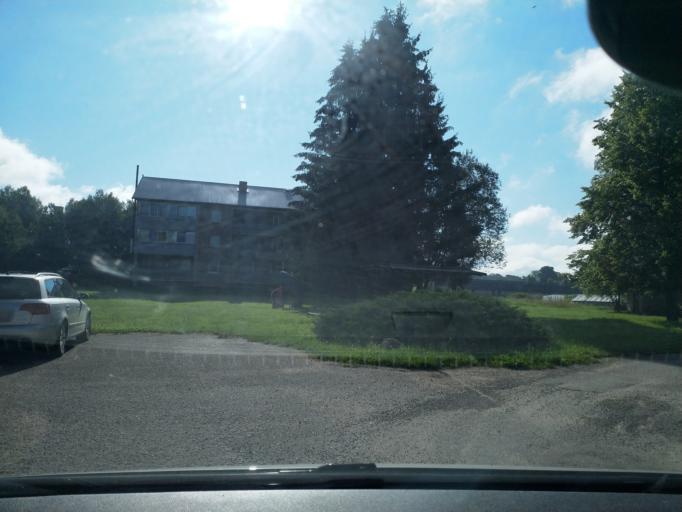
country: LV
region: Kuldigas Rajons
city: Kuldiga
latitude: 56.9656
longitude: 22.0052
